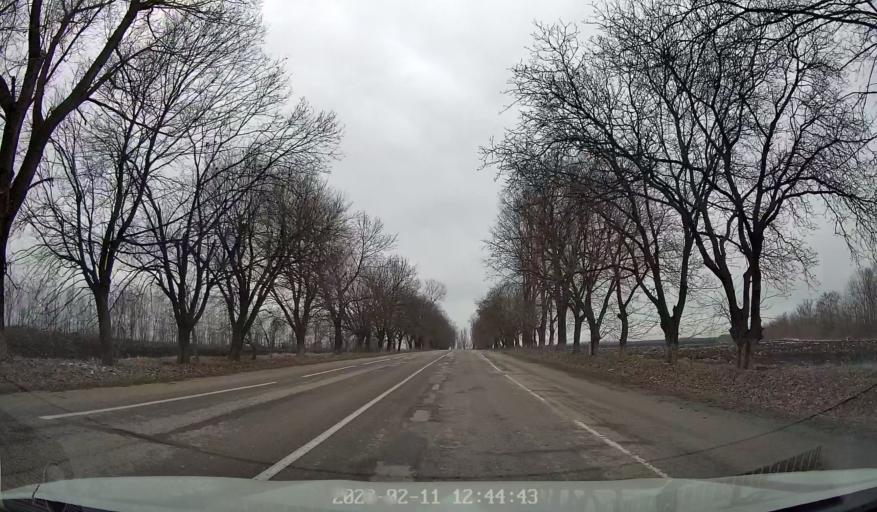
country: MD
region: Raionul Edinet
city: Edinet
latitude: 48.2490
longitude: 27.2004
